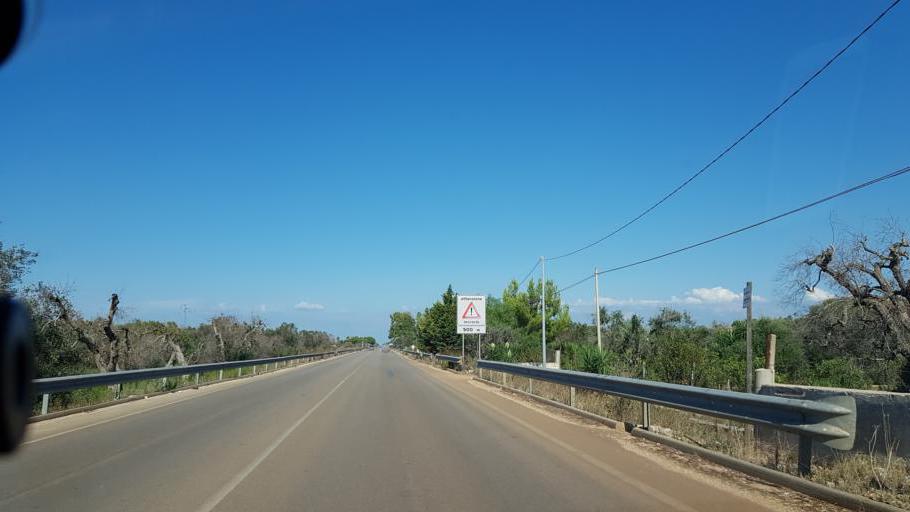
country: IT
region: Apulia
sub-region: Provincia di Lecce
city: Leverano
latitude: 40.2383
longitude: 17.9639
